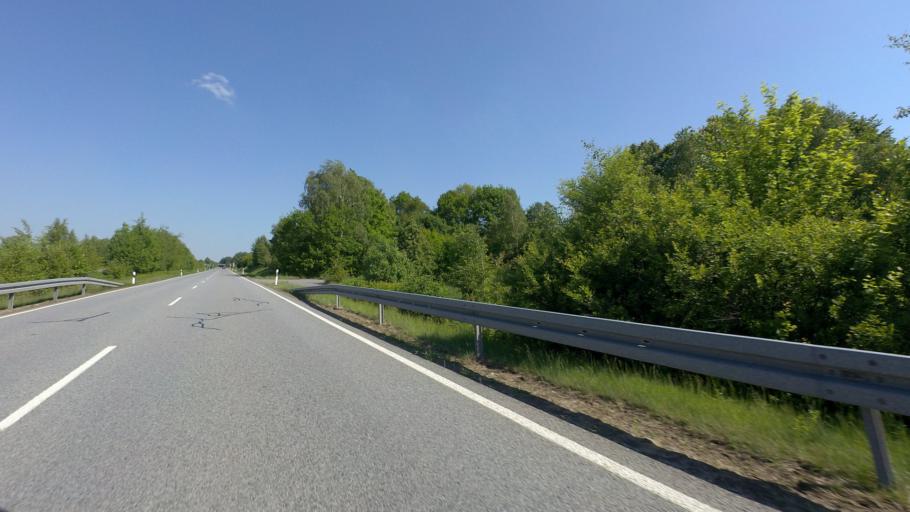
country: DE
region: Saxony
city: Berthelsdorf
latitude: 51.0436
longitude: 14.2135
